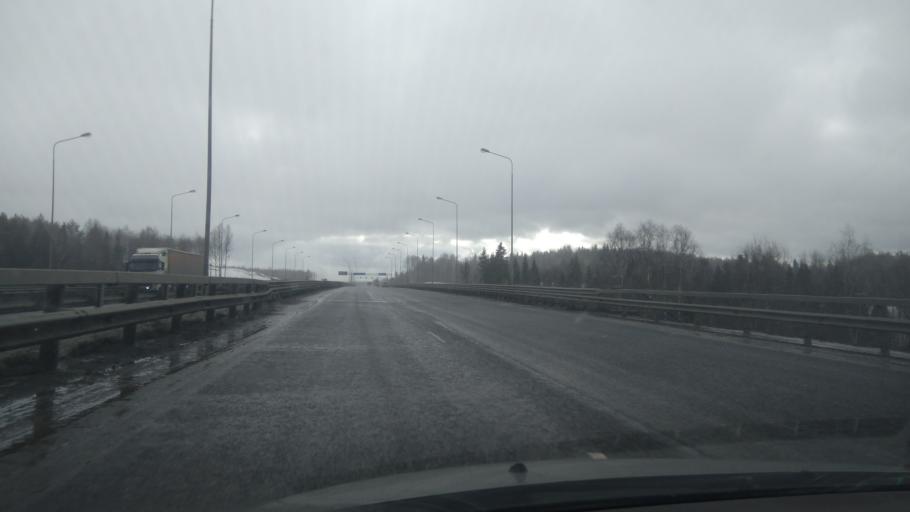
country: RU
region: Perm
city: Zvezdnyy
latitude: 57.7396
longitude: 56.3399
